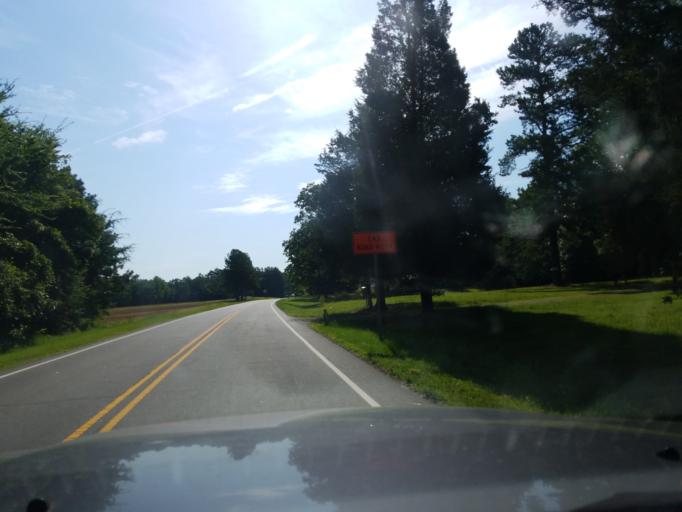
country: US
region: North Carolina
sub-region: Granville County
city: Oxford
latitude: 36.2494
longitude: -78.6834
